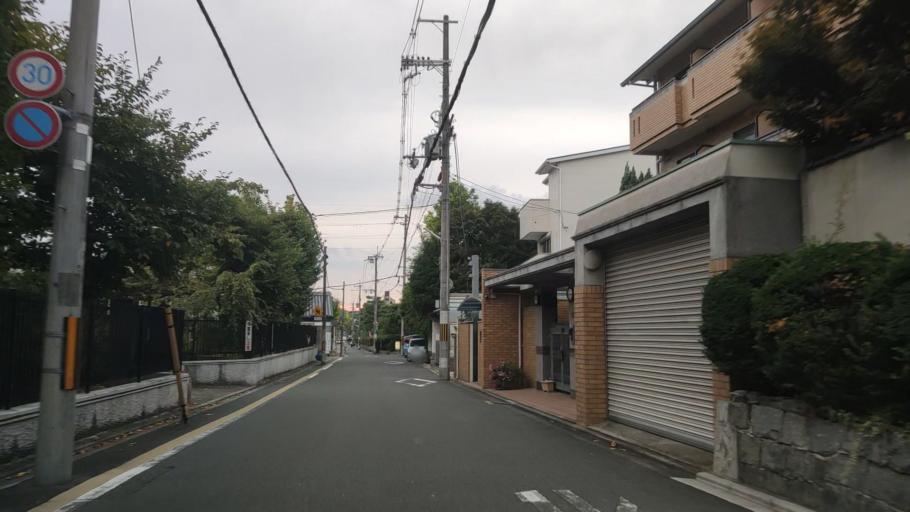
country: JP
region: Kyoto
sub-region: Kyoto-shi
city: Kamigyo-ku
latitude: 35.0186
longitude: 135.7824
